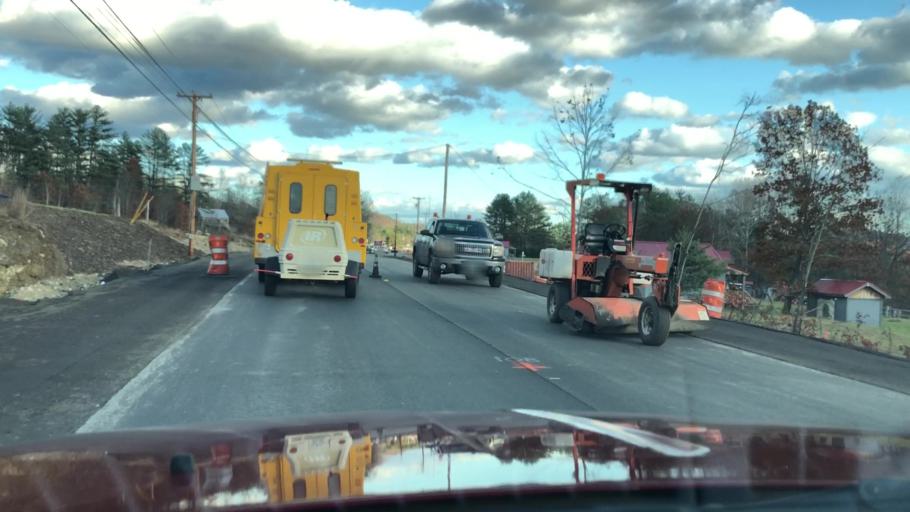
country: US
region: Maine
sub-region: Oxford County
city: Peru
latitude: 44.5190
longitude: -70.4185
